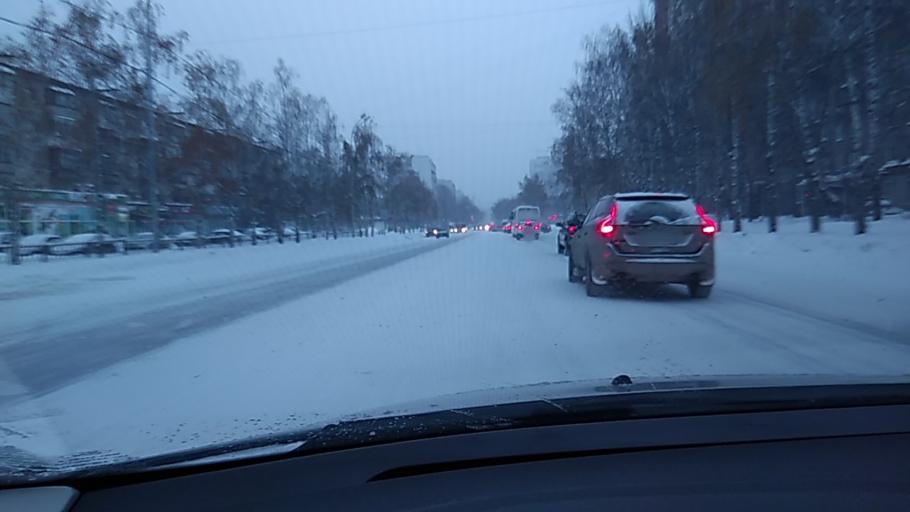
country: RU
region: Sverdlovsk
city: Sovkhoznyy
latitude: 56.8182
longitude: 60.5603
